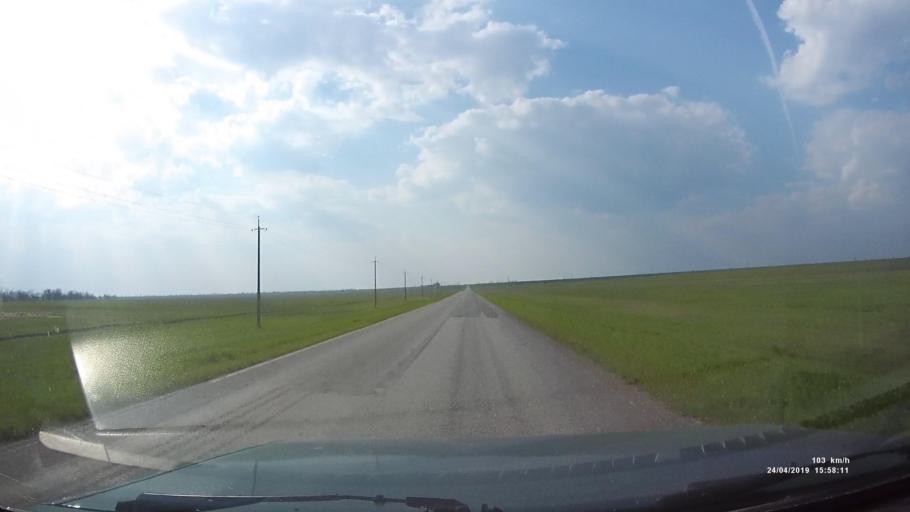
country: RU
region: Kalmykiya
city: Yashalta
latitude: 46.6119
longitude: 42.4948
